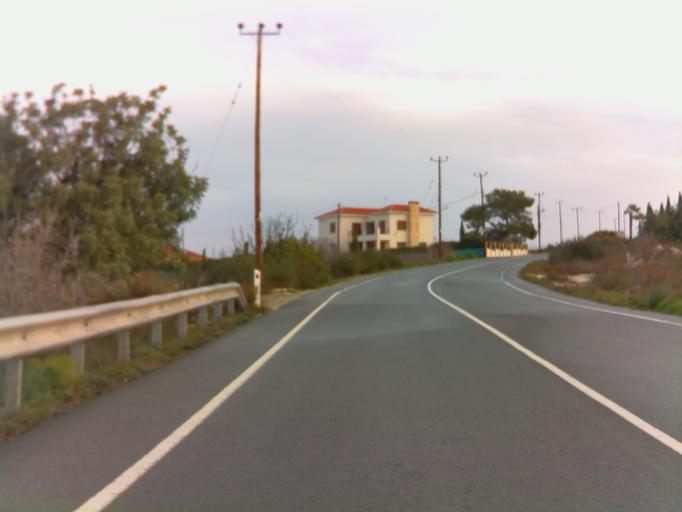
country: CY
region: Pafos
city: Pegeia
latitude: 34.8990
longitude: 32.3880
